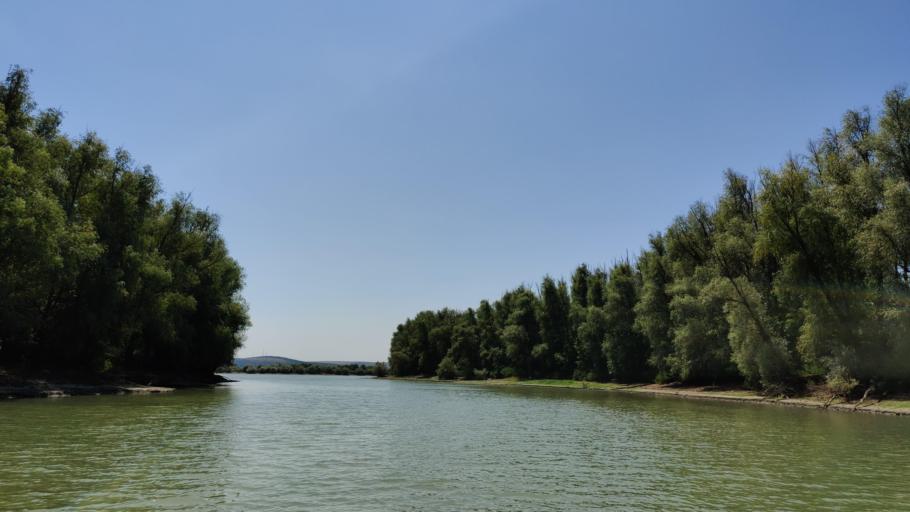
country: RO
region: Tulcea
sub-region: Municipiul Tulcea
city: Tulcea
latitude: 45.2068
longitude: 28.8538
